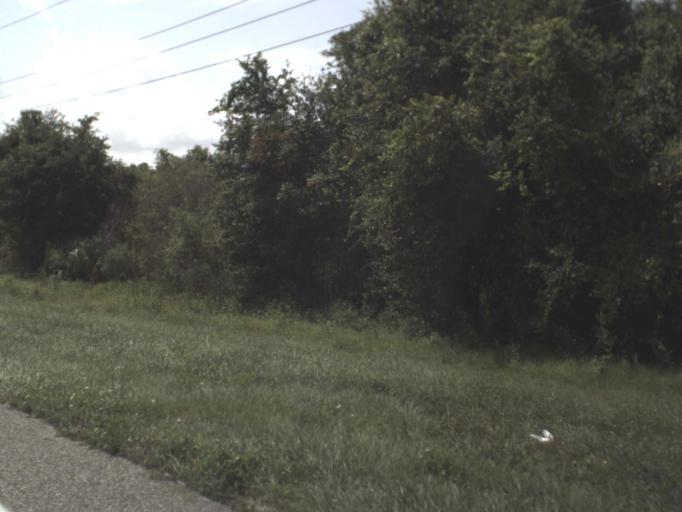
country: US
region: Florida
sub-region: Polk County
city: Crooked Lake Park
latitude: 27.8638
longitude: -81.5904
